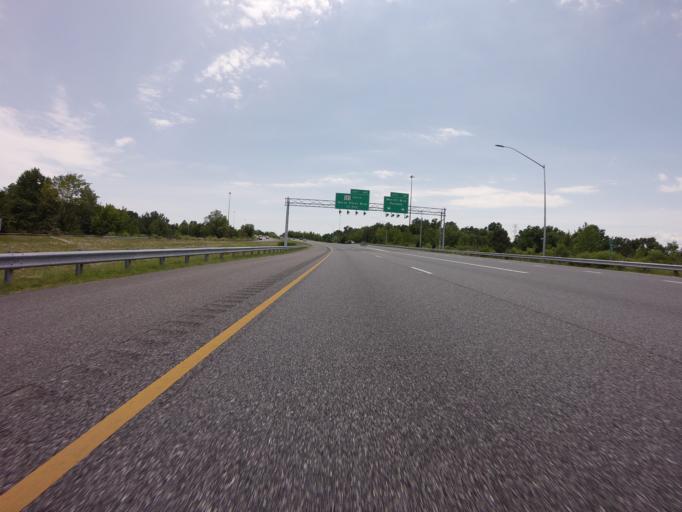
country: US
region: Maryland
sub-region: Baltimore County
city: Rosedale
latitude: 39.2957
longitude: -76.5036
